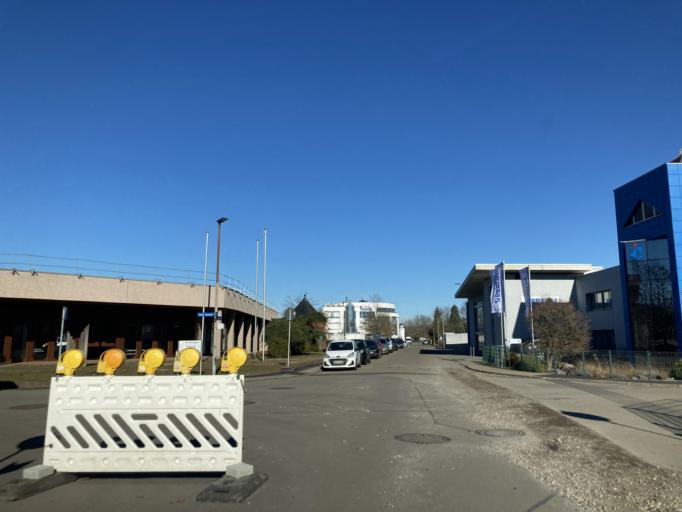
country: DE
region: Baden-Wuerttemberg
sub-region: Freiburg Region
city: Bahlingen
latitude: 48.1220
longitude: 7.7483
